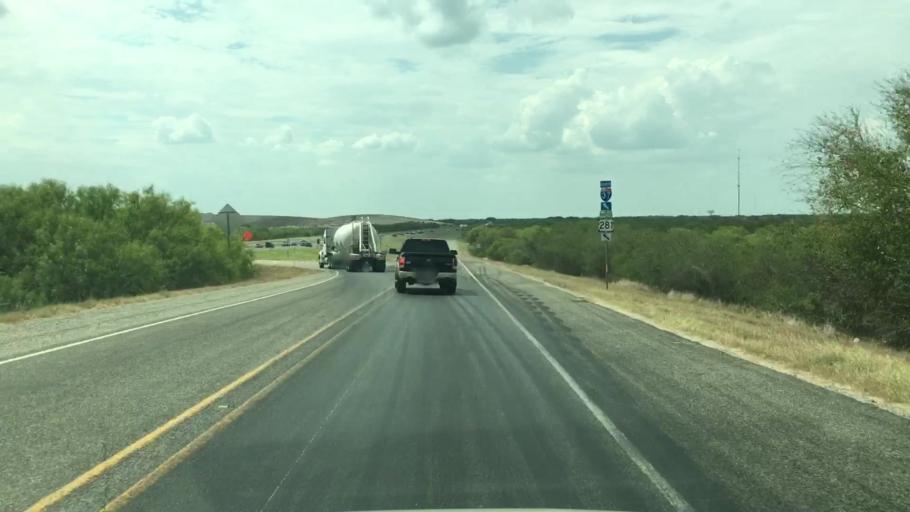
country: US
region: Texas
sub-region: Atascosa County
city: Pleasanton
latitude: 28.7864
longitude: -98.3224
